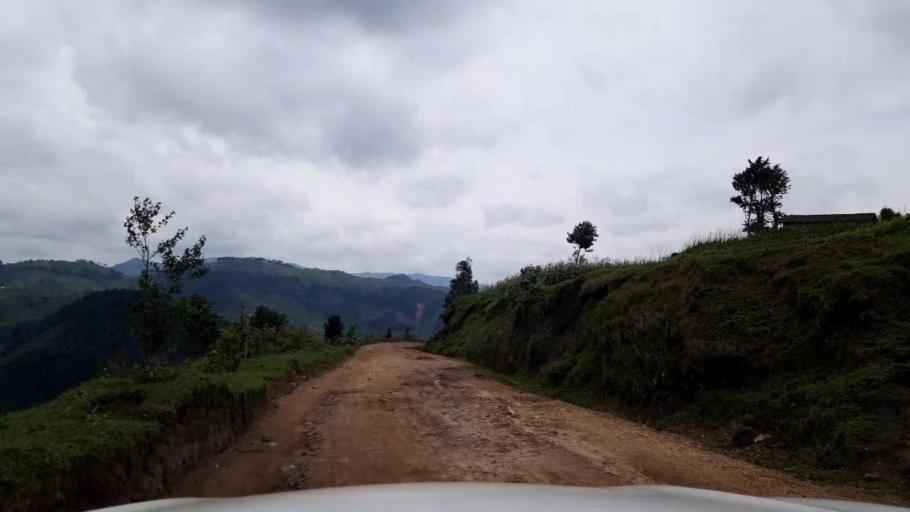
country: RW
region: Western Province
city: Kibuye
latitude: -1.9545
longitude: 29.4200
